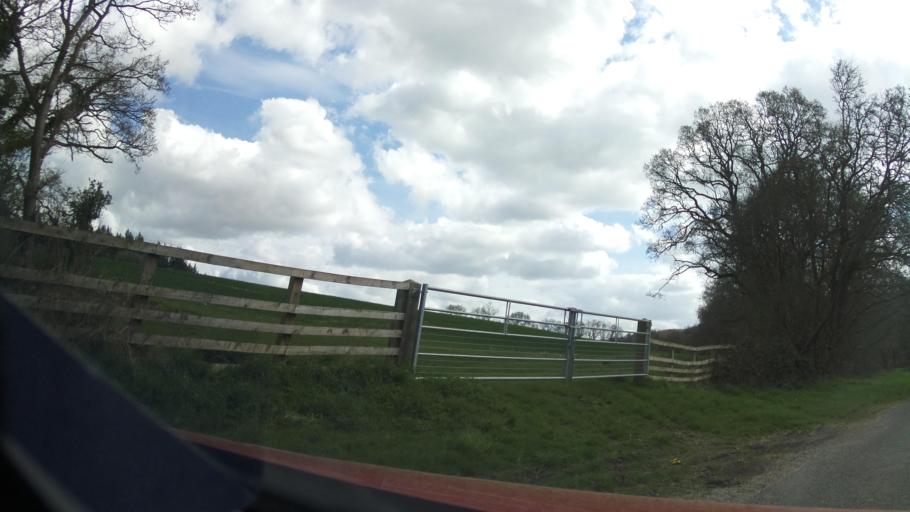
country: GB
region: England
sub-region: Hampshire
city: Highclere
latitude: 51.3108
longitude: -1.4599
